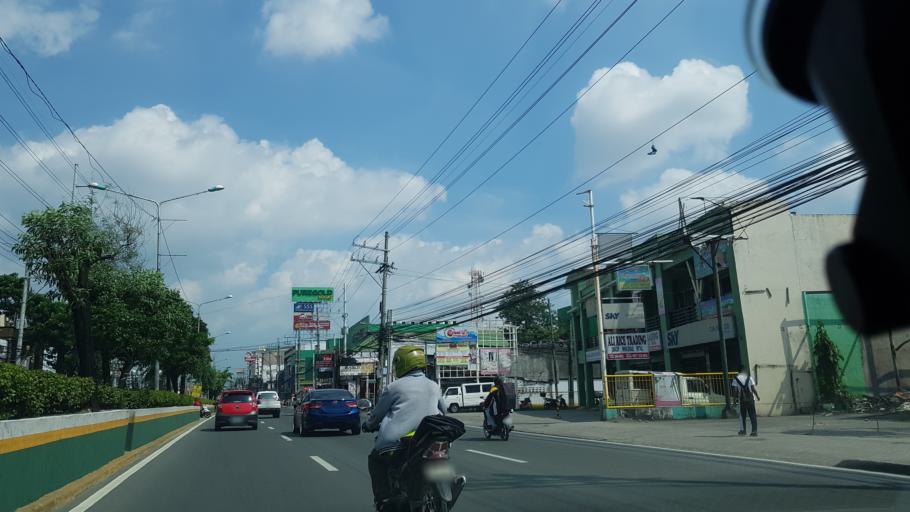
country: PH
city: Sambayanihan People's Village
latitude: 14.4667
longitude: 121.0151
